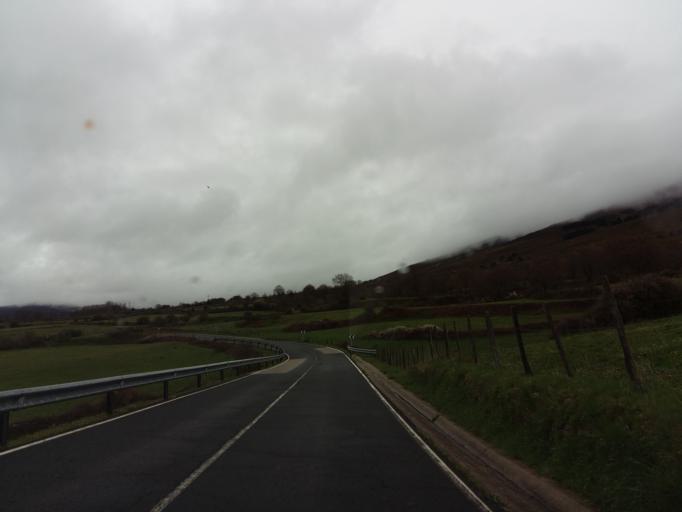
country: ES
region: Cantabria
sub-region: Provincia de Cantabria
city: Villaescusa
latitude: 42.9354
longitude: -4.2066
